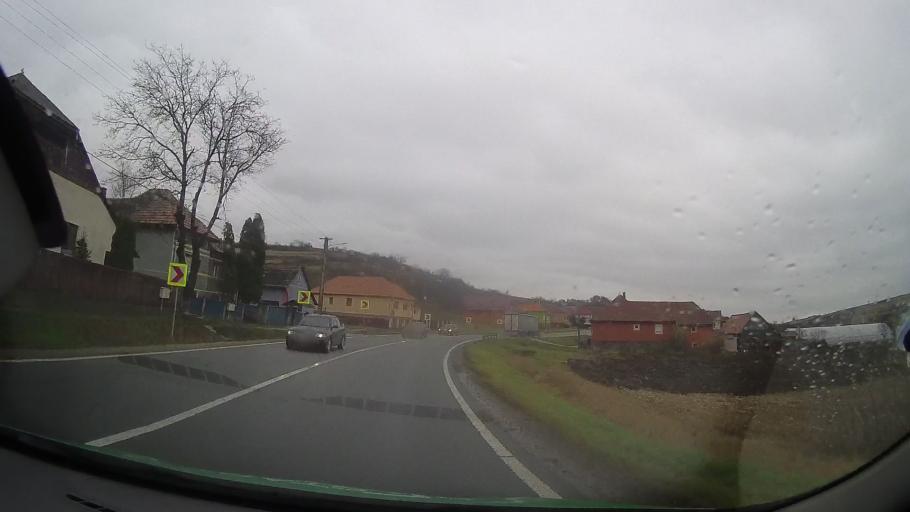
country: RO
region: Mures
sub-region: Comuna Lunca
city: Lunca
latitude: 46.8564
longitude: 24.5676
